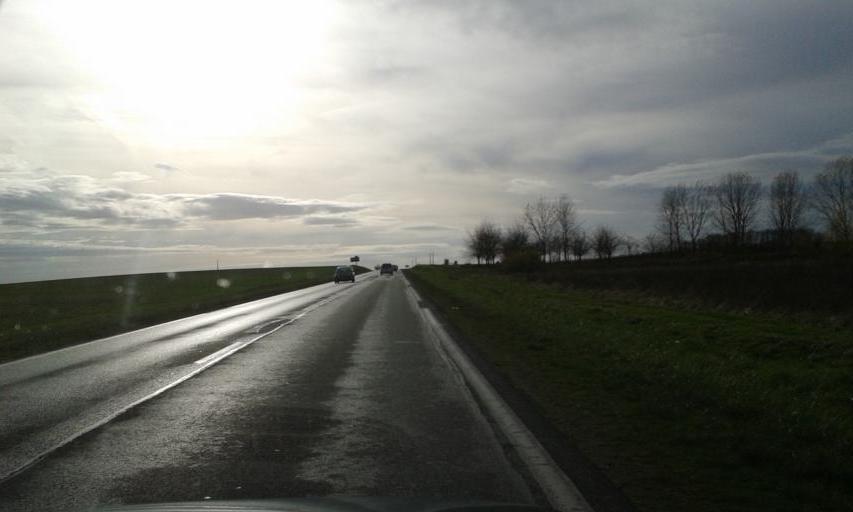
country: FR
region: Centre
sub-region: Departement du Loiret
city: Baule
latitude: 47.7977
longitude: 1.6534
